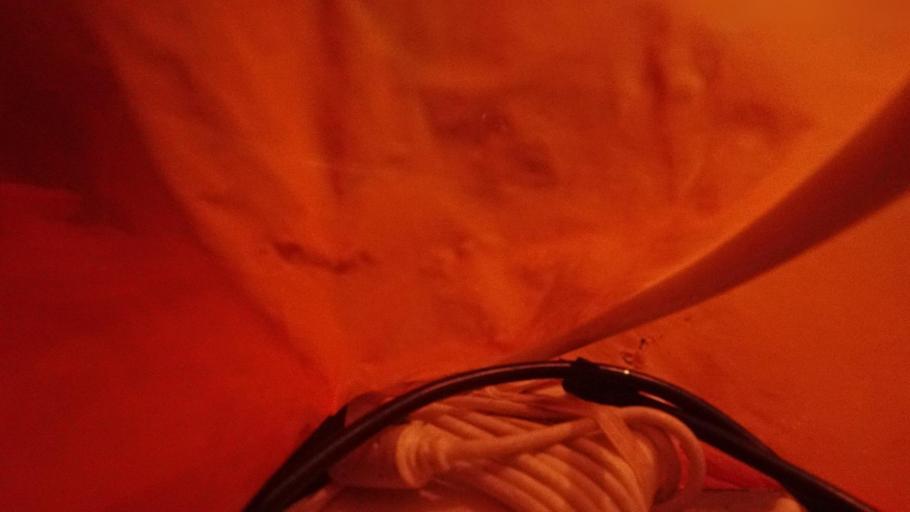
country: RU
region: Jewish Autonomous Oblast
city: Khingansk
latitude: 49.1637
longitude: 130.7825
